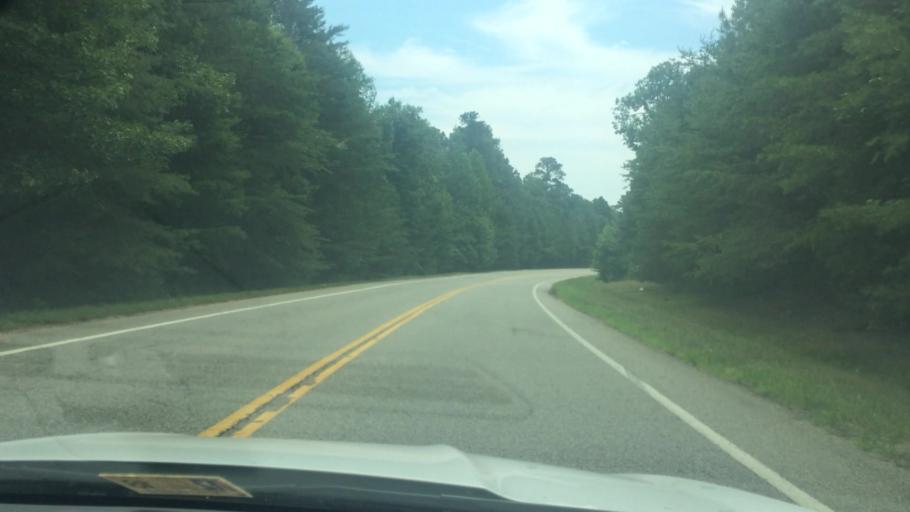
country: US
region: Virginia
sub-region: James City County
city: Williamsburg
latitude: 37.2682
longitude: -76.8066
